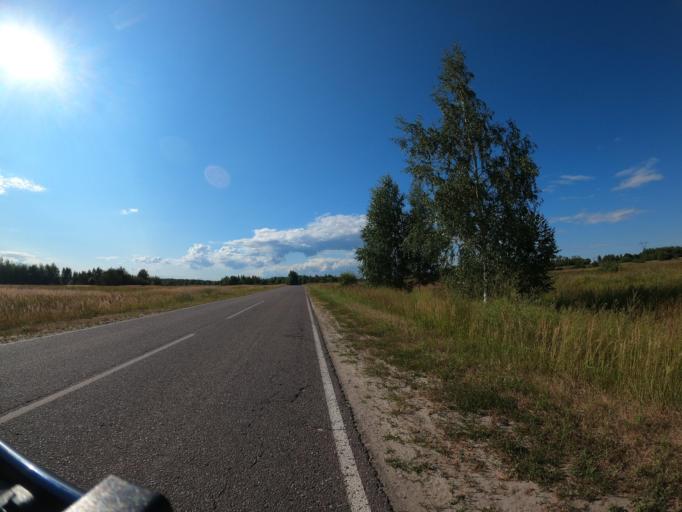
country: RU
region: Moskovskaya
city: Konobeyevo
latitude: 55.3994
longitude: 38.7128
